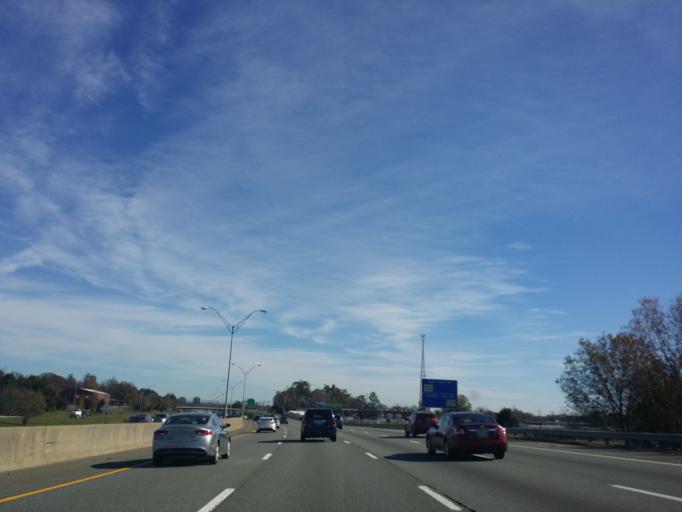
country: US
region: North Carolina
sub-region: Alamance County
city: Graham
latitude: 36.0598
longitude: -79.3995
